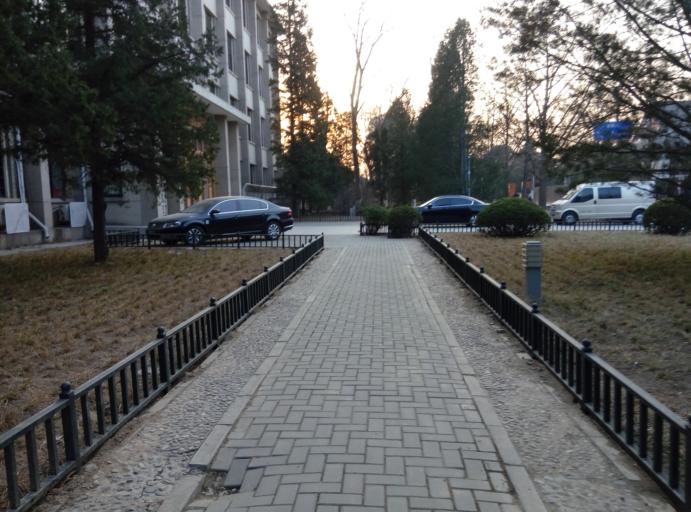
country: CN
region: Beijing
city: Haidian
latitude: 39.9911
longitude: 116.3038
